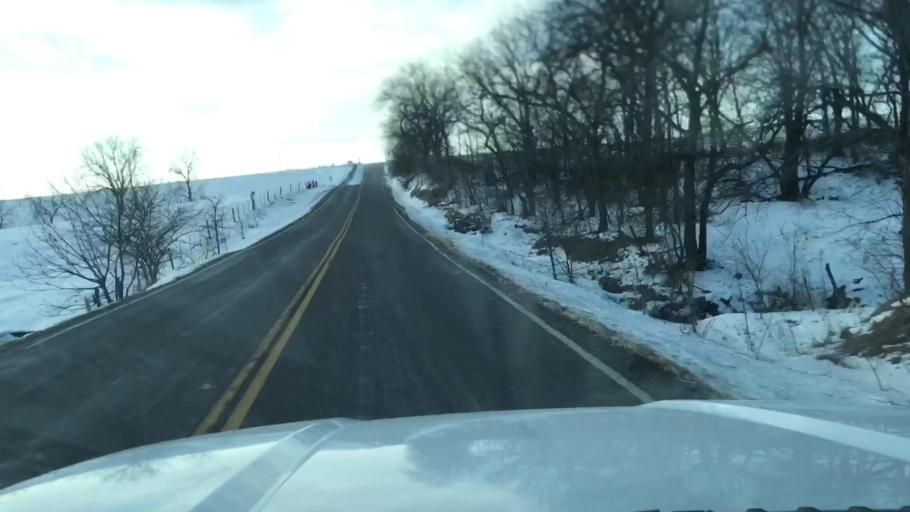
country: US
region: Missouri
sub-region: Nodaway County
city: Maryville
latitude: 40.2020
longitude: -94.9482
